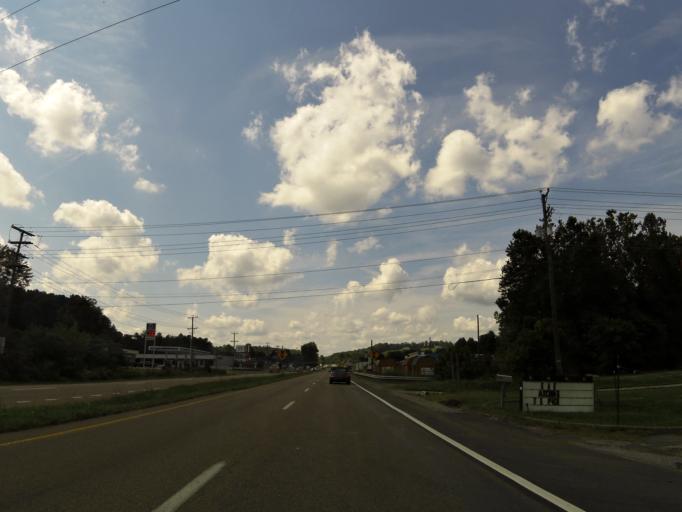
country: US
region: Virginia
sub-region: Washington County
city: Abingdon
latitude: 36.7192
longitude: -82.0096
